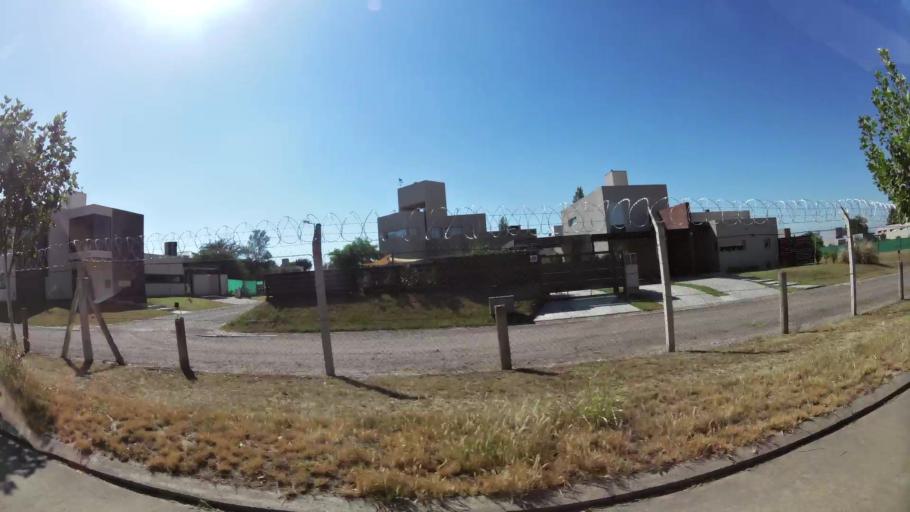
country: AR
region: Cordoba
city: Villa Allende
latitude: -31.3047
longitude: -64.2646
